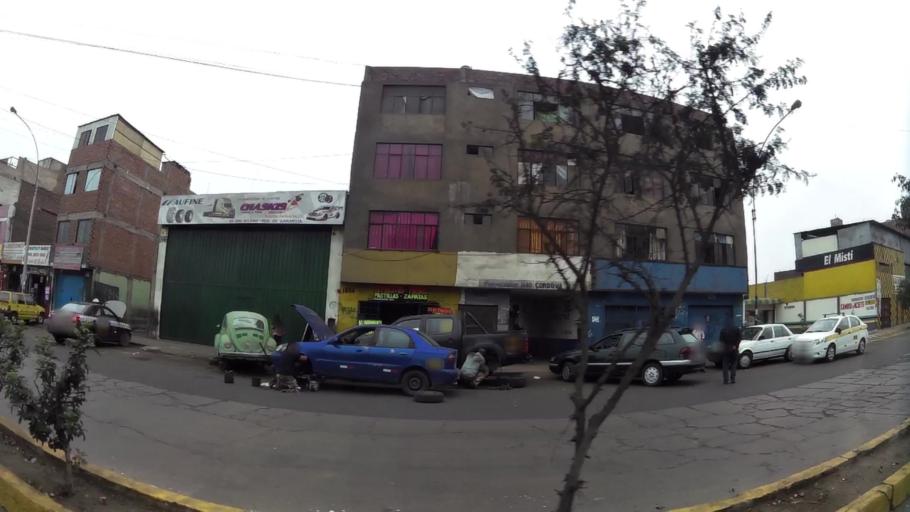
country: PE
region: Lima
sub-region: Lima
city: San Luis
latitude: -12.0751
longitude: -77.0165
